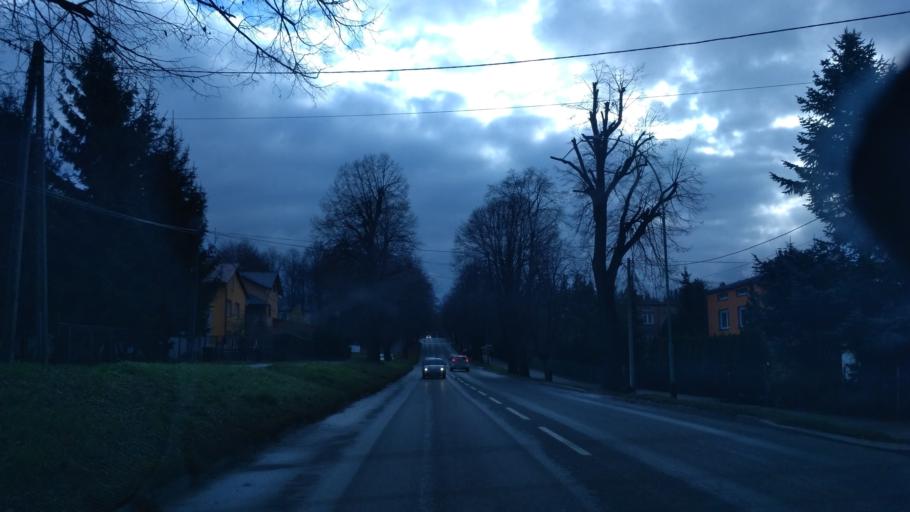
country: PL
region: Subcarpathian Voivodeship
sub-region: Powiat lancucki
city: Lancut
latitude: 50.0746
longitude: 22.2367
